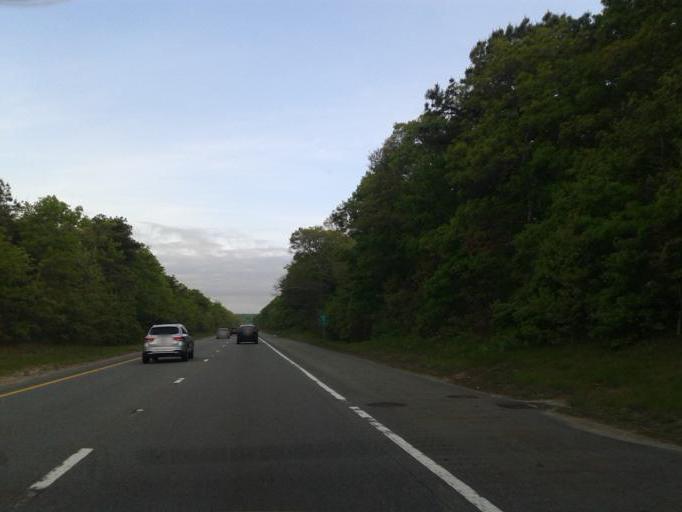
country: US
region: Massachusetts
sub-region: Barnstable County
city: North Falmouth
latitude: 41.6523
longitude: -70.6030
